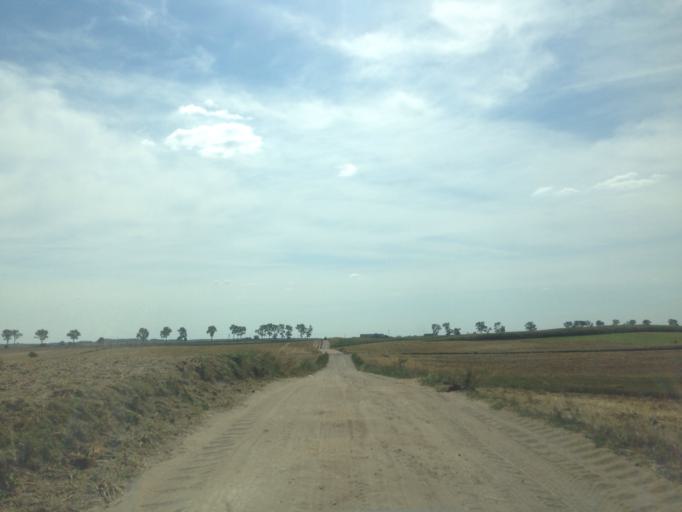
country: PL
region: Kujawsko-Pomorskie
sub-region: Powiat brodnicki
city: Gorzno
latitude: 53.2046
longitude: 19.6226
